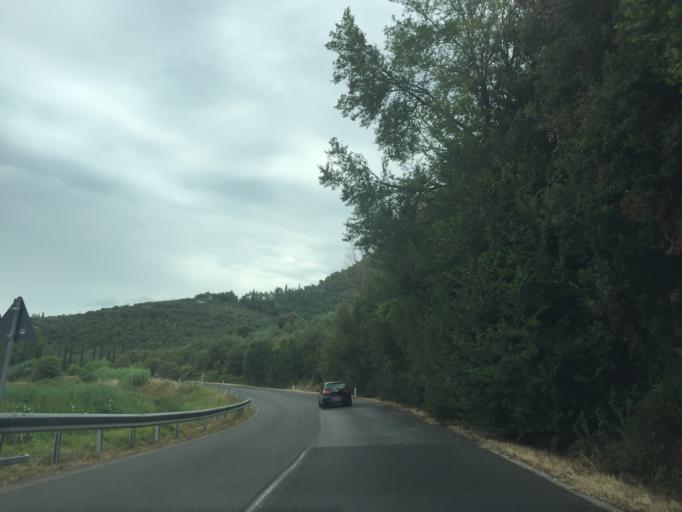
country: IT
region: Tuscany
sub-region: Province of Pisa
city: Asciano
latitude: 43.7377
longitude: 10.4734
